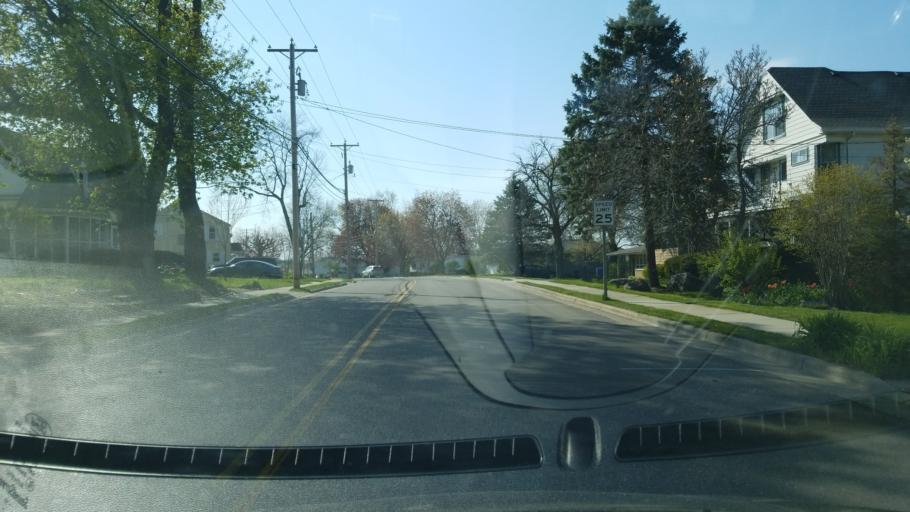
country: US
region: Wisconsin
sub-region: Dane County
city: Oregon
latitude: 42.9287
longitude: -89.3912
